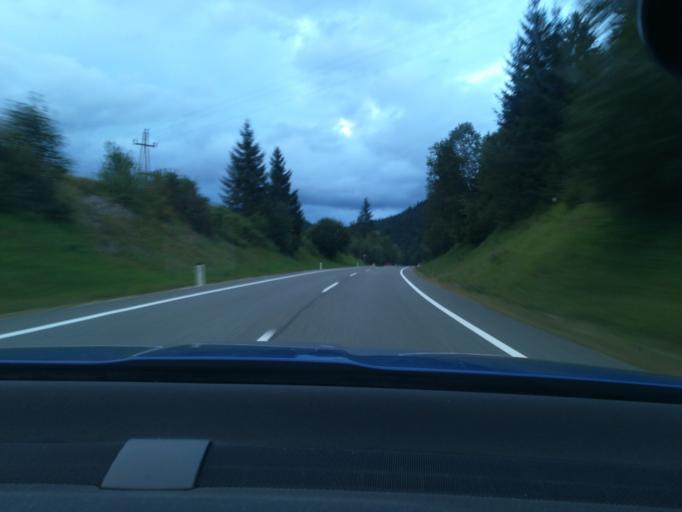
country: AT
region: Salzburg
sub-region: Politischer Bezirk Salzburg-Umgebung
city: Strobl
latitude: 47.5920
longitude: 13.4921
